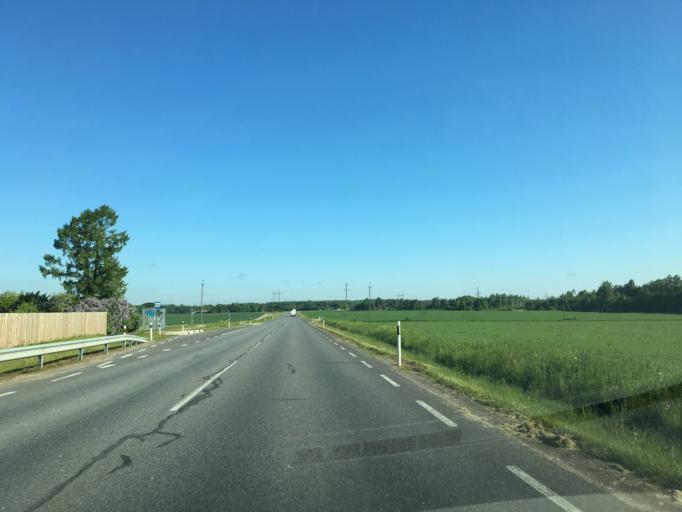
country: EE
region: Tartu
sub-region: Tartu linn
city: Tartu
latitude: 58.4447
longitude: 26.6799
